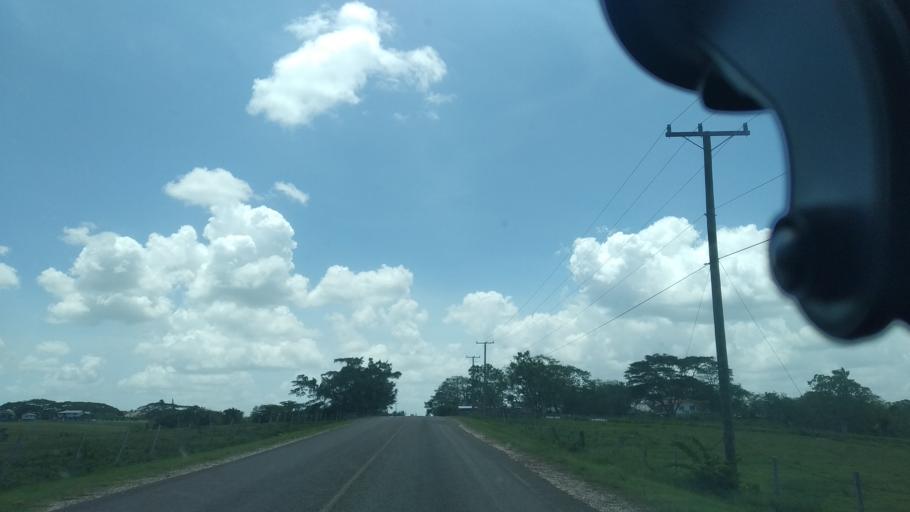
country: BZ
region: Cayo
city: San Ignacio
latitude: 17.2511
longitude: -88.9874
